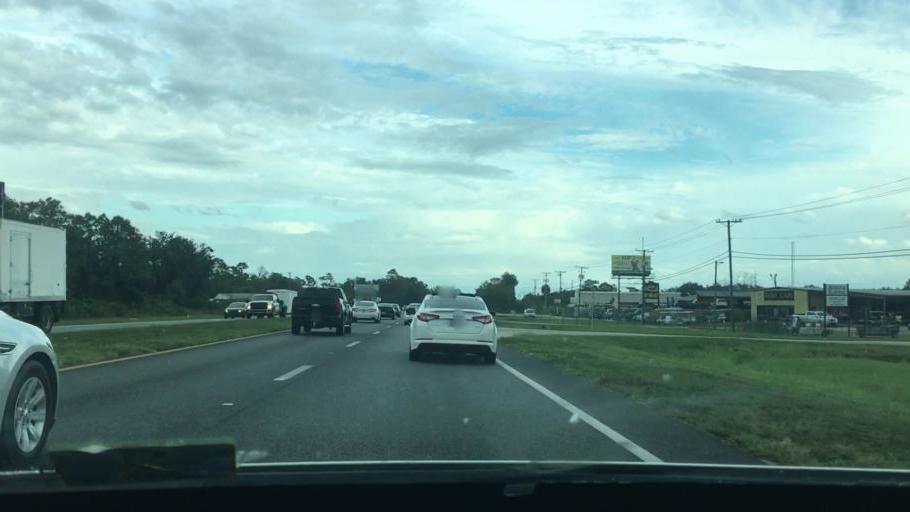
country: US
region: Florida
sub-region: Orange County
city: Bithlo
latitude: 28.5510
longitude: -81.0996
